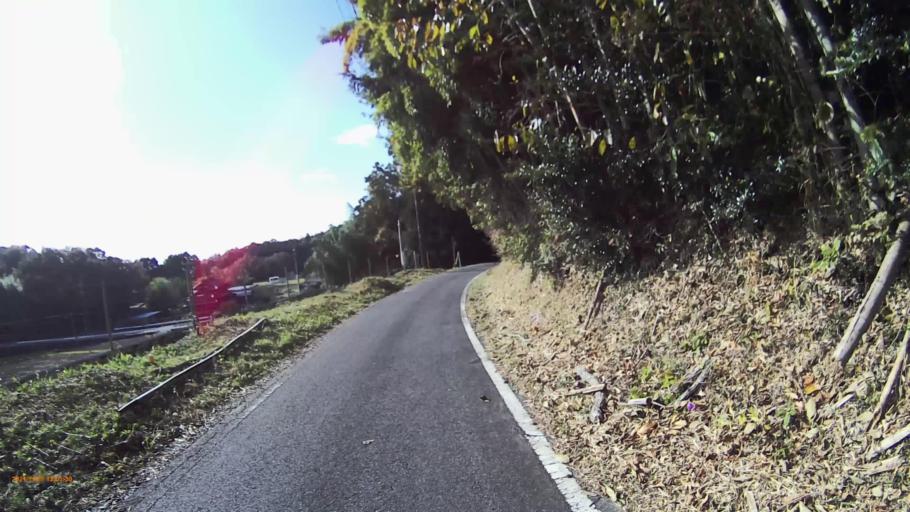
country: JP
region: Gifu
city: Mizunami
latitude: 35.4272
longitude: 137.2230
